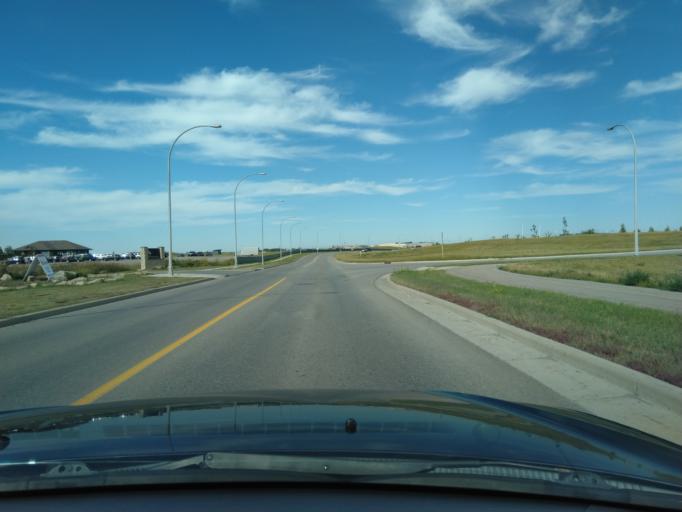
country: CA
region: Alberta
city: Calgary
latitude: 51.0981
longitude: -113.9871
